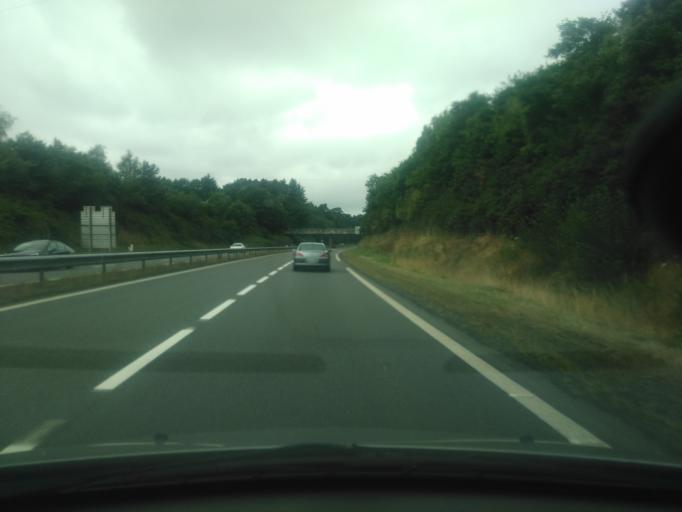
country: FR
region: Brittany
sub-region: Departement des Cotes-d'Armor
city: Plelan-le-Petit
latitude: 48.4245
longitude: -2.2128
